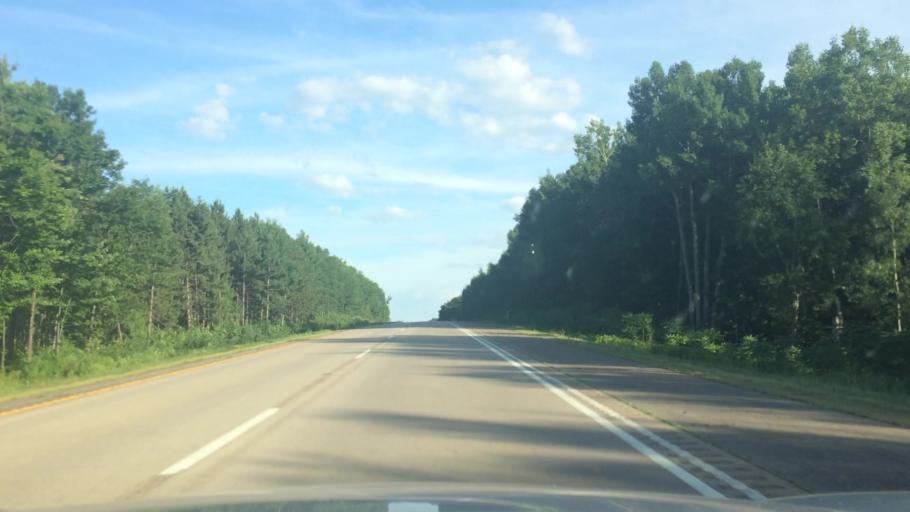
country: US
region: Wisconsin
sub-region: Marathon County
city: Mosinee
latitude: 44.7066
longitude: -89.6555
